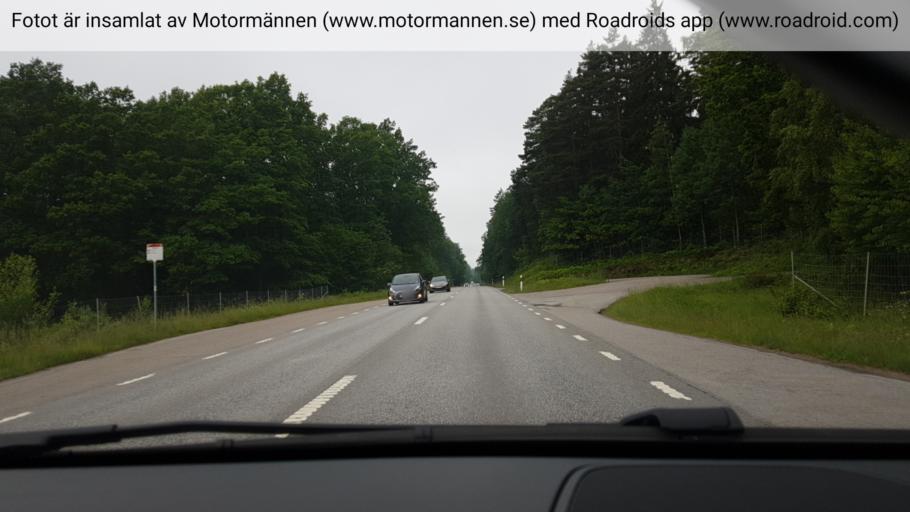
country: SE
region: OEstergoetland
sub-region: Motala Kommun
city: Borensberg
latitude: 58.5700
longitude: 15.2509
